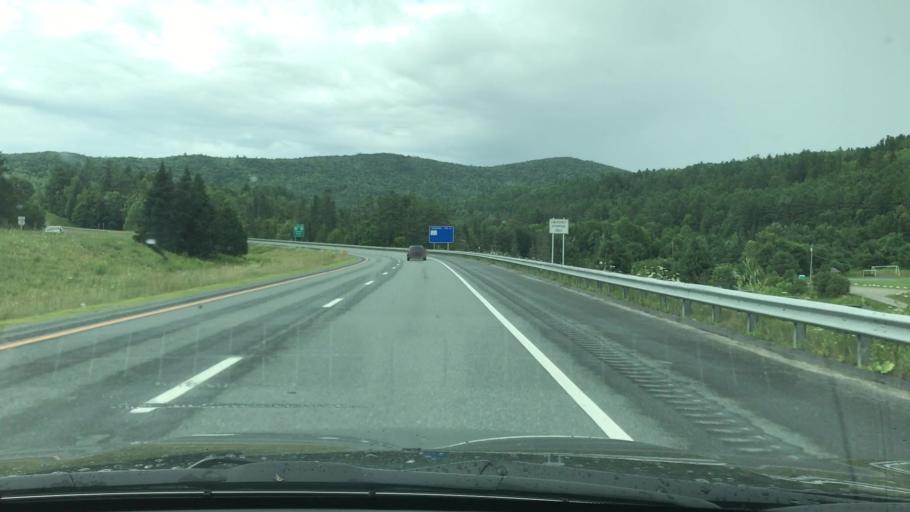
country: US
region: New Hampshire
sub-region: Grafton County
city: Littleton
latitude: 44.3197
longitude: -71.7965
